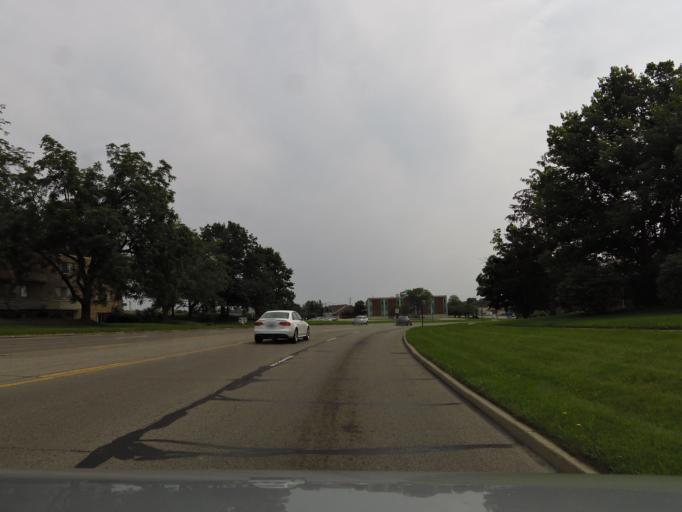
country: US
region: Ohio
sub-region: Montgomery County
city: Kettering
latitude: 39.6955
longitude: -84.1269
